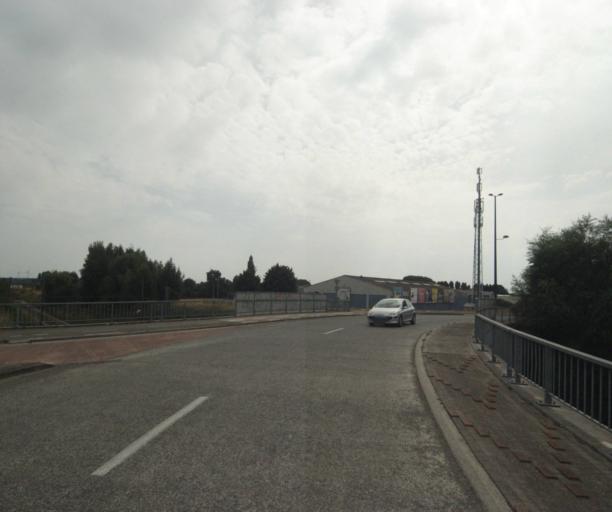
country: BE
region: Wallonia
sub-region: Province du Hainaut
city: Estaimpuis
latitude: 50.7088
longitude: 3.2553
